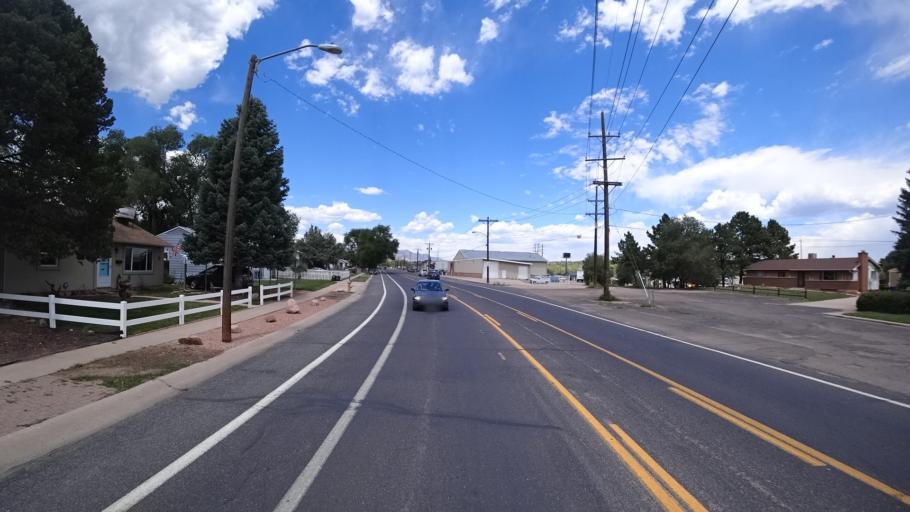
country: US
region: Colorado
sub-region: El Paso County
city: Colorado Springs
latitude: 38.8037
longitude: -104.8037
